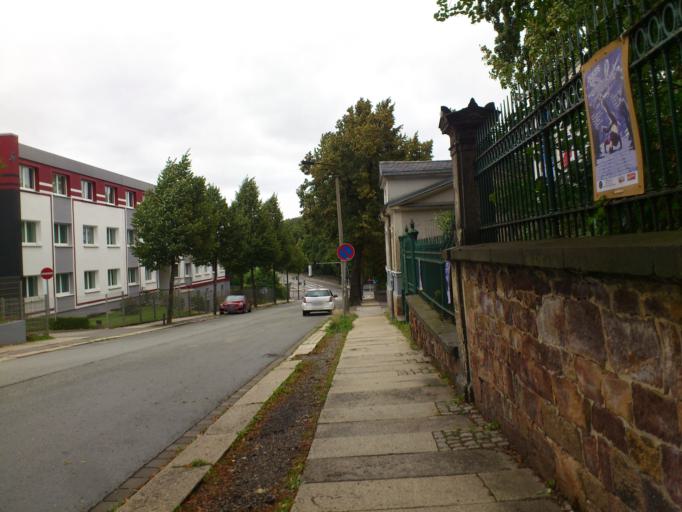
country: DE
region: Saxony
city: Chemnitz
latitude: 50.8373
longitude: 12.9098
